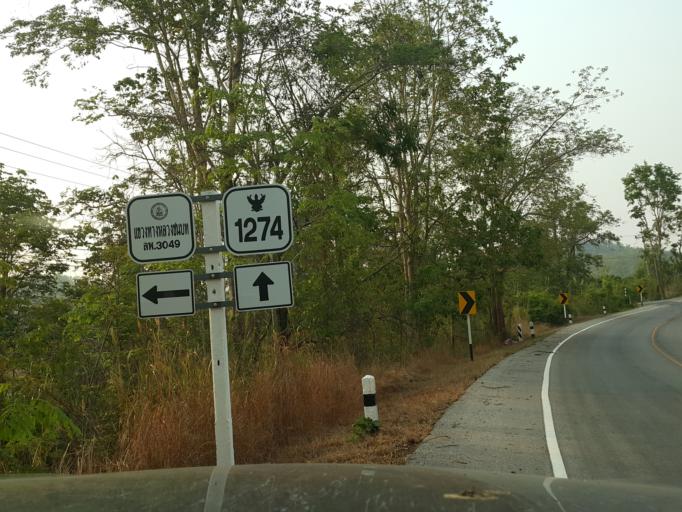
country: TH
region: Lamphun
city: Li
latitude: 17.8397
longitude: 98.9892
